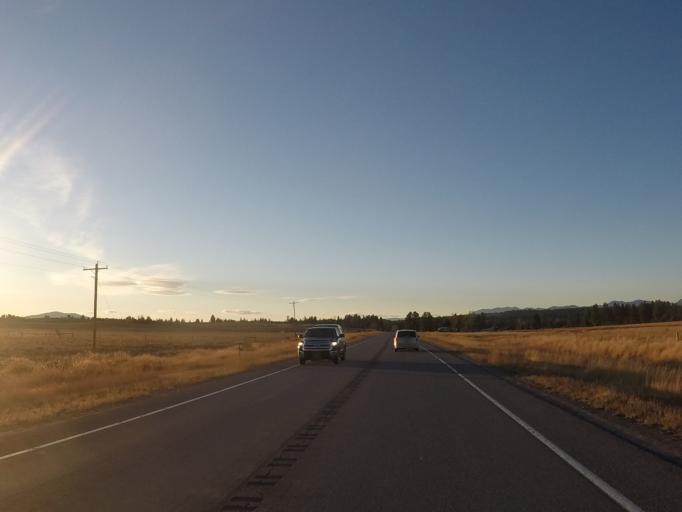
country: US
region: Montana
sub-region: Lewis and Clark County
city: Lincoln
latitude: 46.9933
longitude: -113.0206
